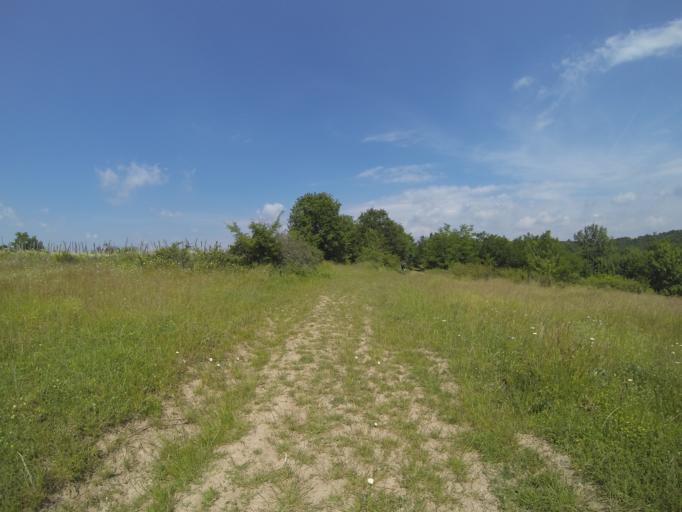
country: RO
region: Gorj
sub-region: Comuna Crusetu
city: Crusetu
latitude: 44.6213
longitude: 23.6199
